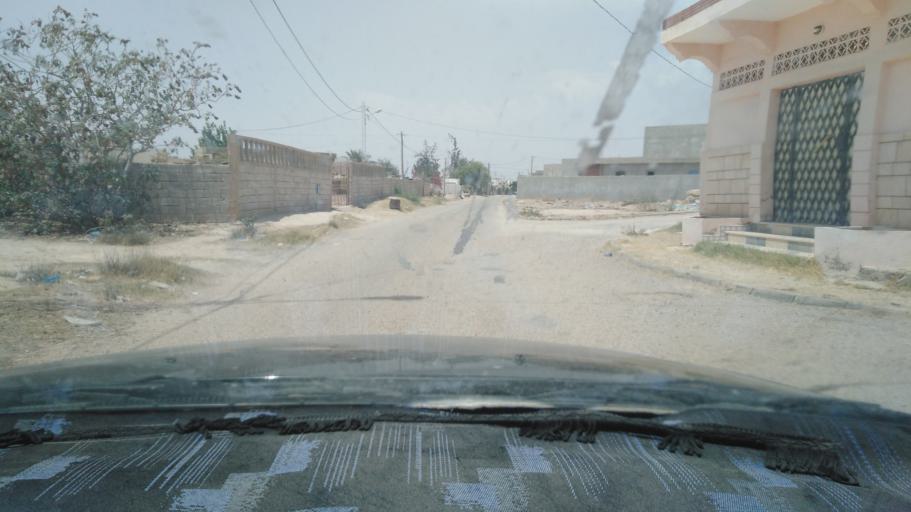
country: TN
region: Qabis
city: Matmata
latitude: 33.6167
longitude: 10.2745
